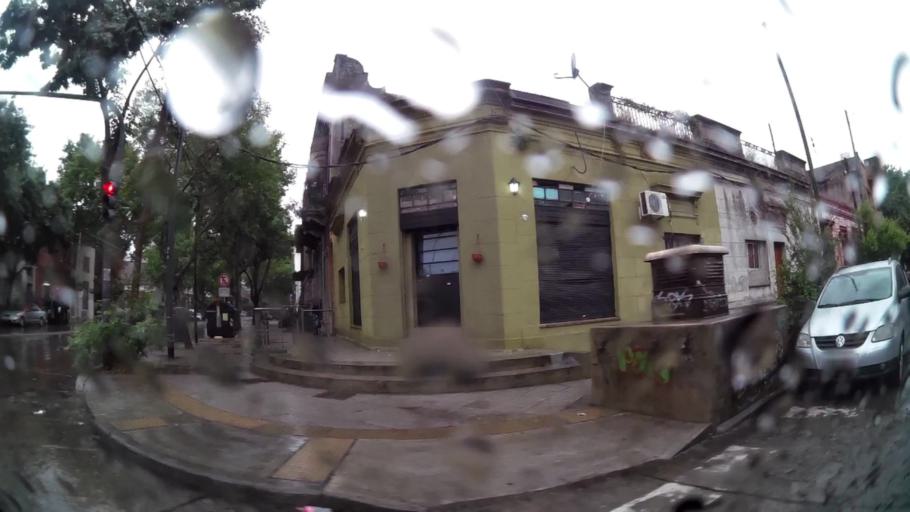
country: AR
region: Buenos Aires
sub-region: Partido de Avellaneda
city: Avellaneda
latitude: -34.6479
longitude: -58.3680
